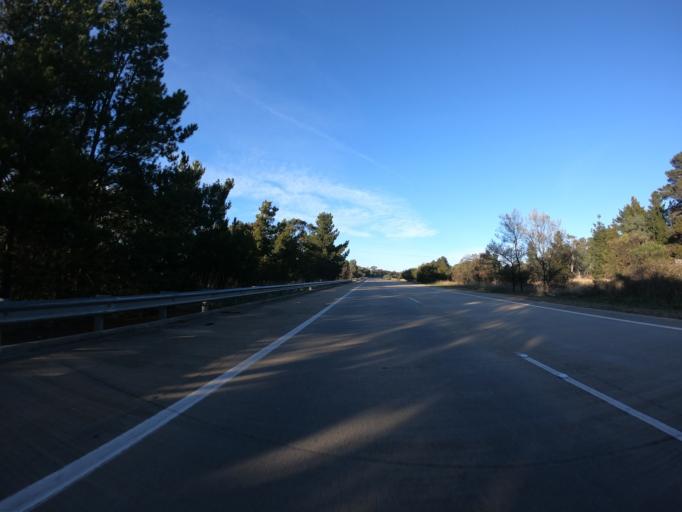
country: AU
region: New South Wales
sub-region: Yass Valley
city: Gundaroo
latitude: -35.1495
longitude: 149.3313
